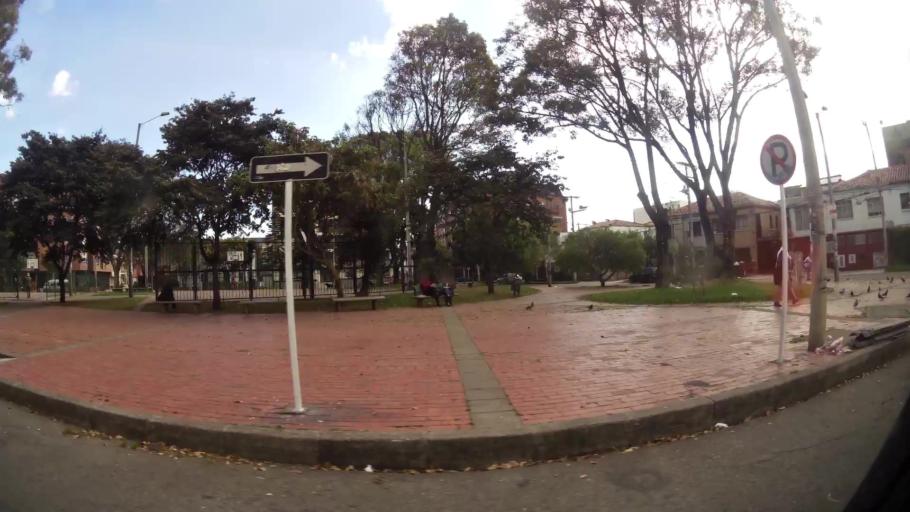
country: CO
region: Bogota D.C.
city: Bogota
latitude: 4.6430
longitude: -74.0703
